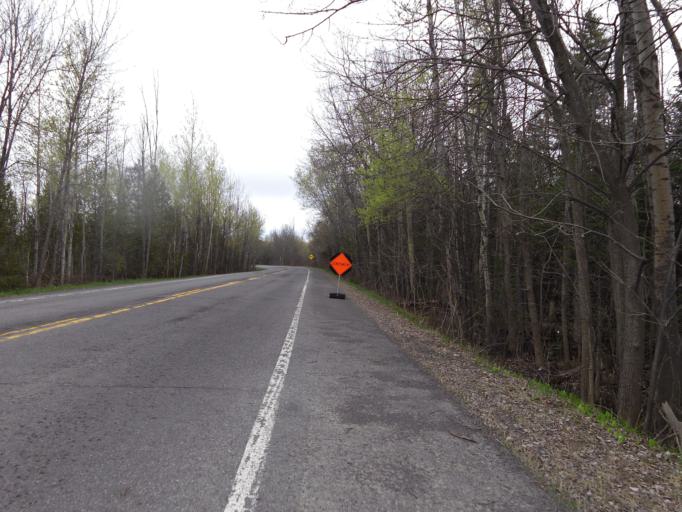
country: CA
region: Quebec
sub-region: Laurentides
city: Lachute
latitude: 45.5739
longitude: -74.3742
